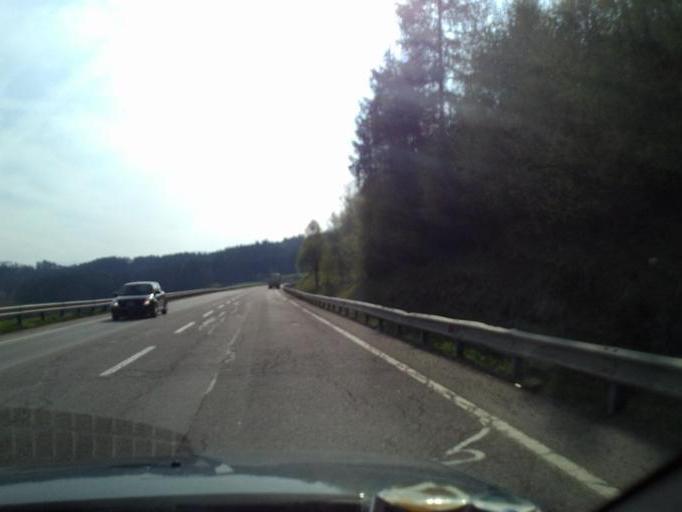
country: IT
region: Trentino-Alto Adige
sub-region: Bolzano
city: San Lorenzo di Sebato
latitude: 46.7811
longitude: 11.9139
